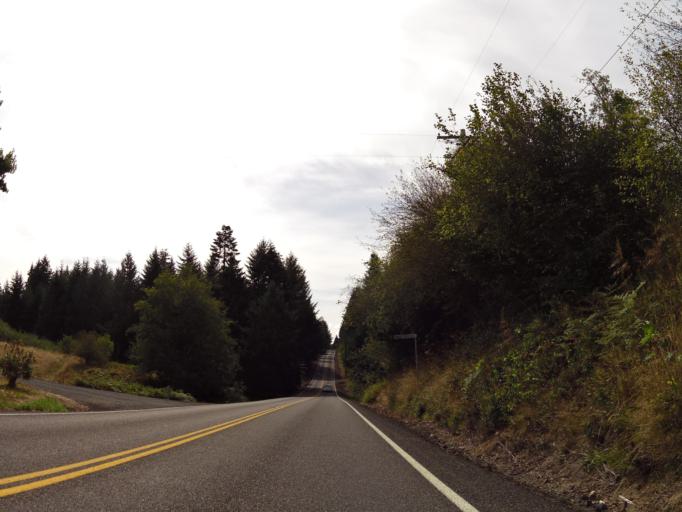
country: US
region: Washington
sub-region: Lewis County
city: Chehalis
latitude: 46.6054
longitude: -122.9713
